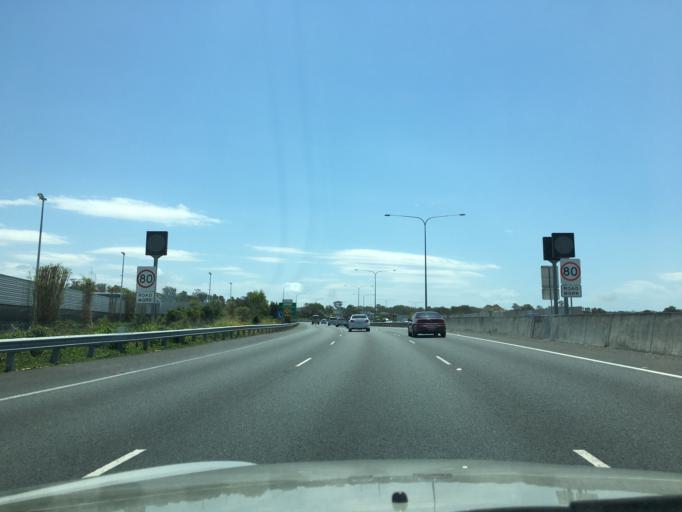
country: AU
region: Queensland
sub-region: Brisbane
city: Wavell Heights
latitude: -27.3835
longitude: 153.0953
